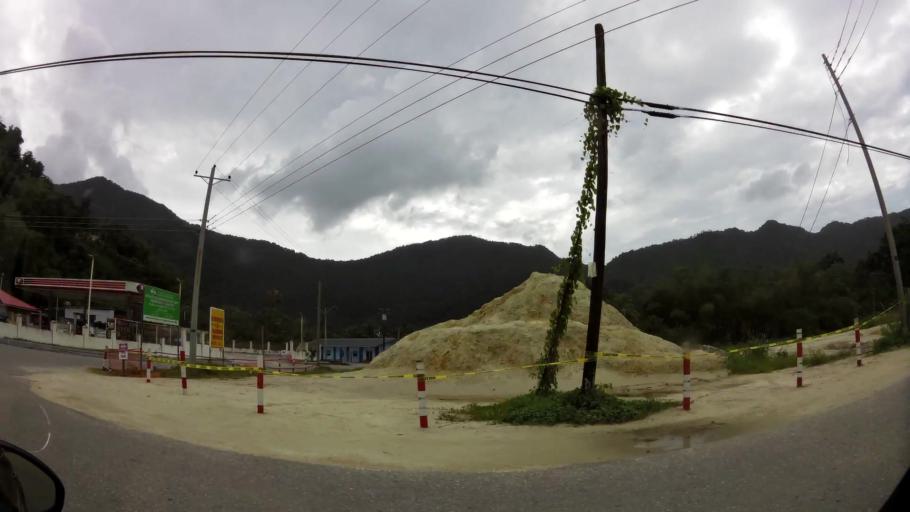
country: TT
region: Diego Martin
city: Petit Valley
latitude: 10.7575
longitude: -61.4372
